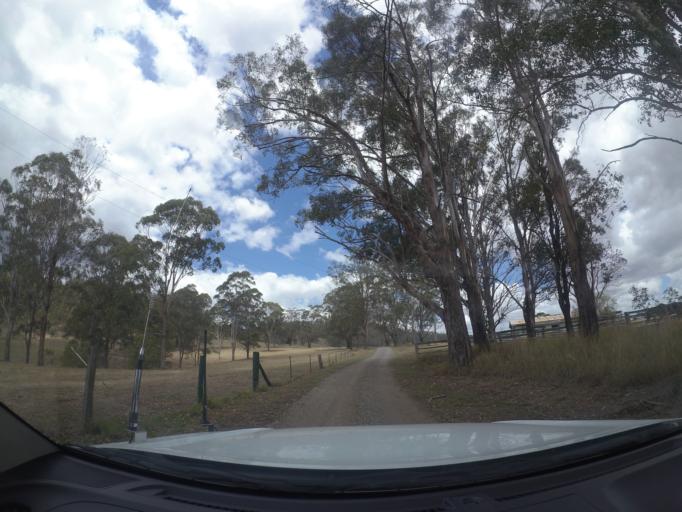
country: AU
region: Queensland
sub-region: Logan
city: Cedar Vale
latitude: -27.9162
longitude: 153.0314
